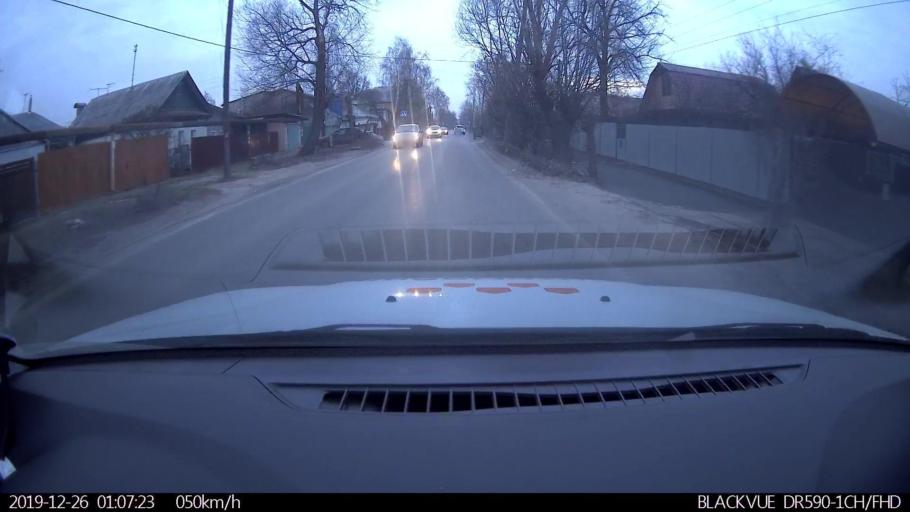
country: RU
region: Nizjnij Novgorod
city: Nizhniy Novgorod
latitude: 56.2812
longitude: 43.9090
